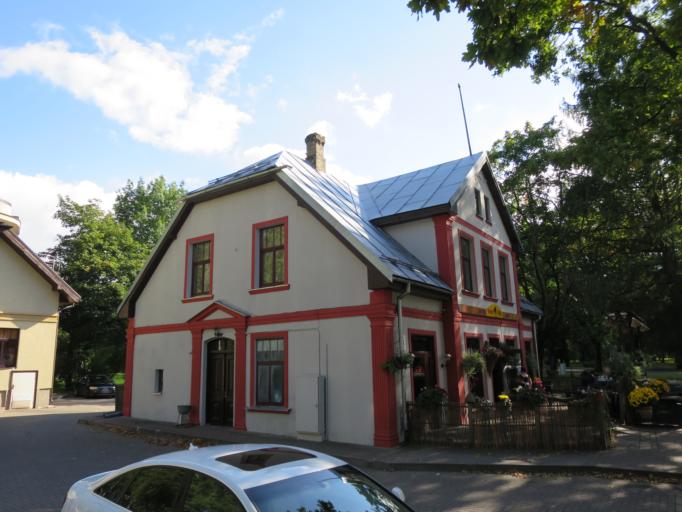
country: LV
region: Sigulda
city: Sigulda
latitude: 57.1564
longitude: 24.8511
